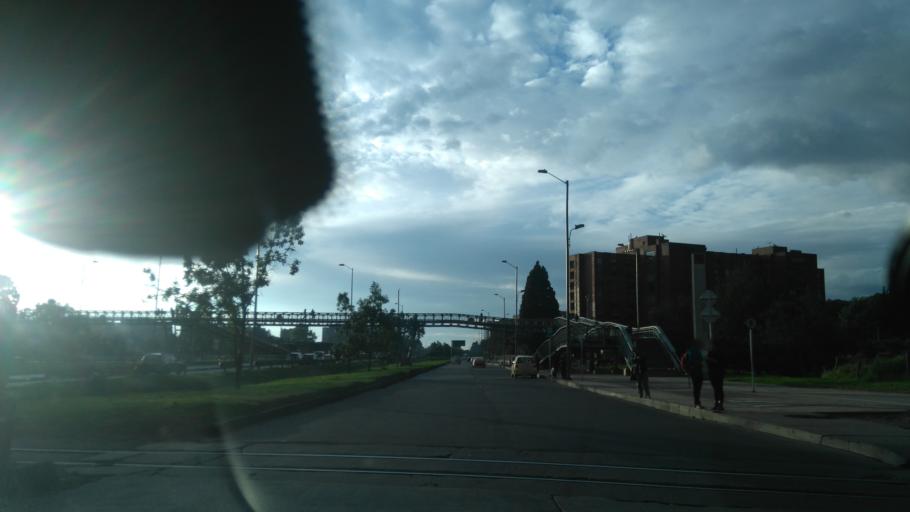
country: CO
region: Bogota D.C.
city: Bogota
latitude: 4.6495
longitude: -74.1004
